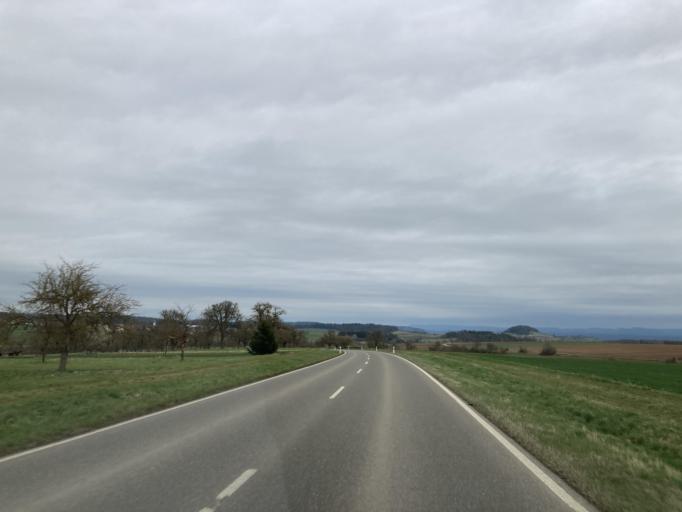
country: DE
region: Baden-Wuerttemberg
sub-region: Regierungsbezirk Stuttgart
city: Bondorf
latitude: 48.5012
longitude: 8.8582
